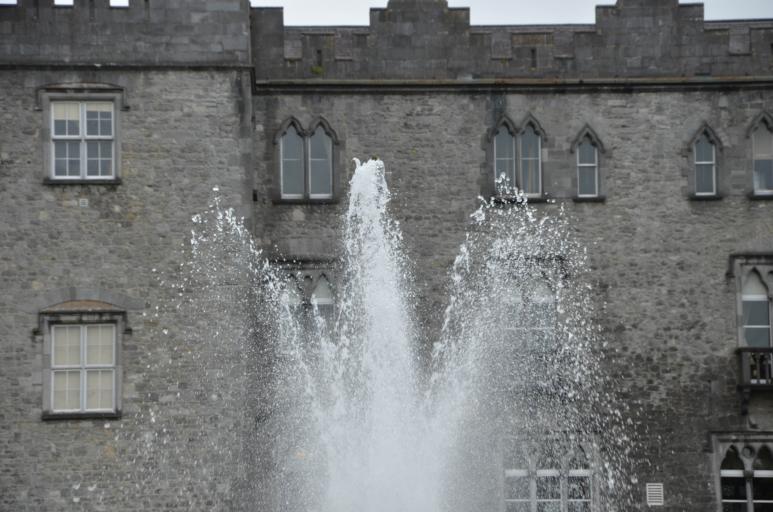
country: IE
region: Leinster
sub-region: Kilkenny
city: Kilkenny
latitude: 52.6509
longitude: -7.2505
